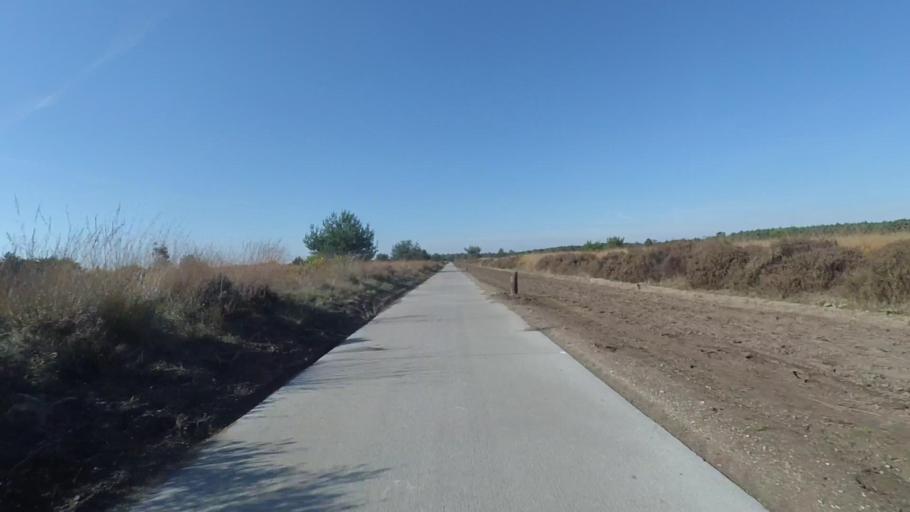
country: NL
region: Gelderland
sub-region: Gemeente Barneveld
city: Stroe
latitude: 52.1865
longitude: 5.7268
